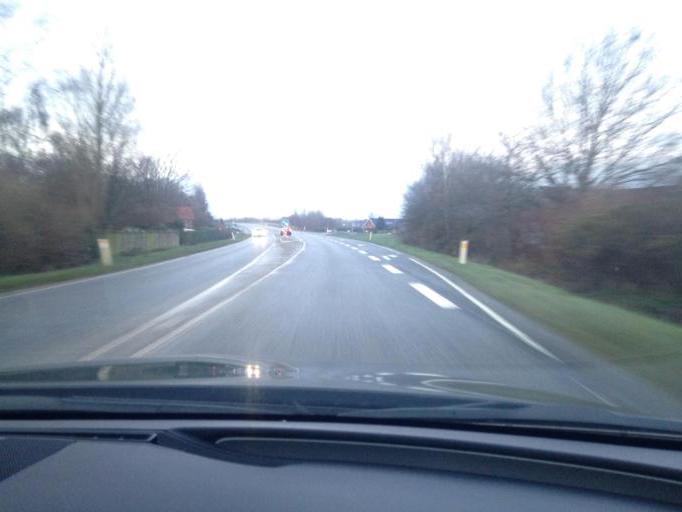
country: DK
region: South Denmark
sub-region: Kolding Kommune
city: Kolding
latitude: 55.5633
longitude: 9.4948
